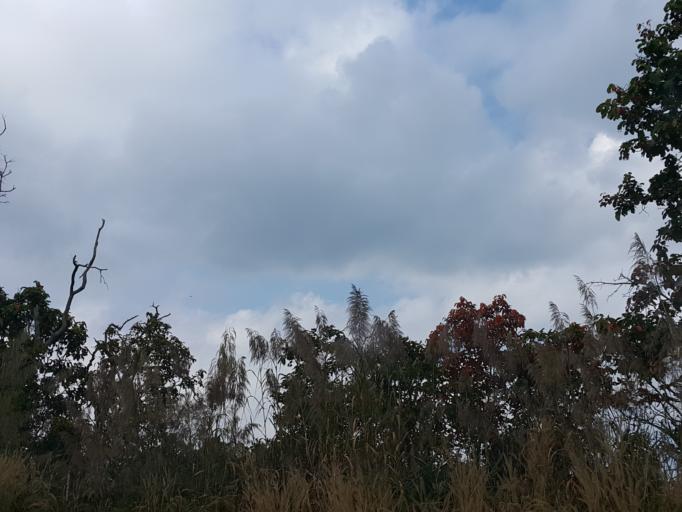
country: TH
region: Chiang Mai
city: Om Koi
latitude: 17.8043
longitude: 98.3626
